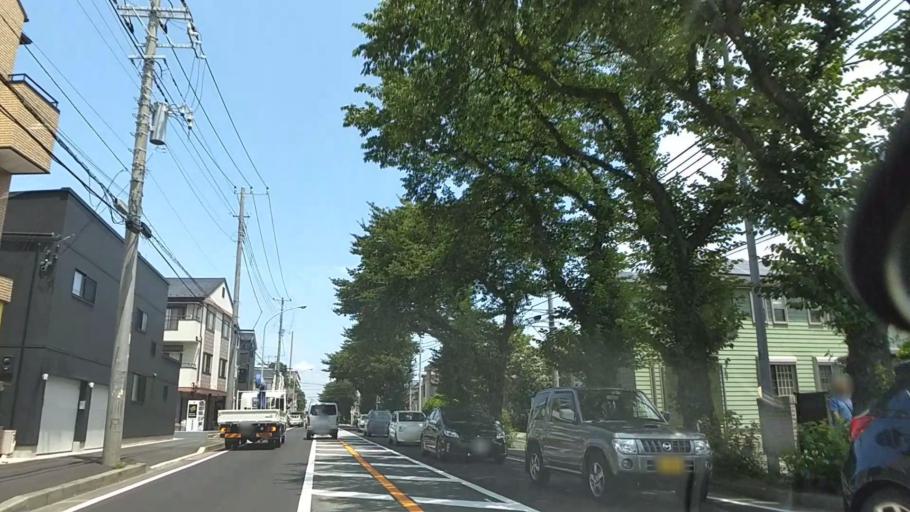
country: JP
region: Kanagawa
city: Minami-rinkan
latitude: 35.4735
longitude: 139.4807
